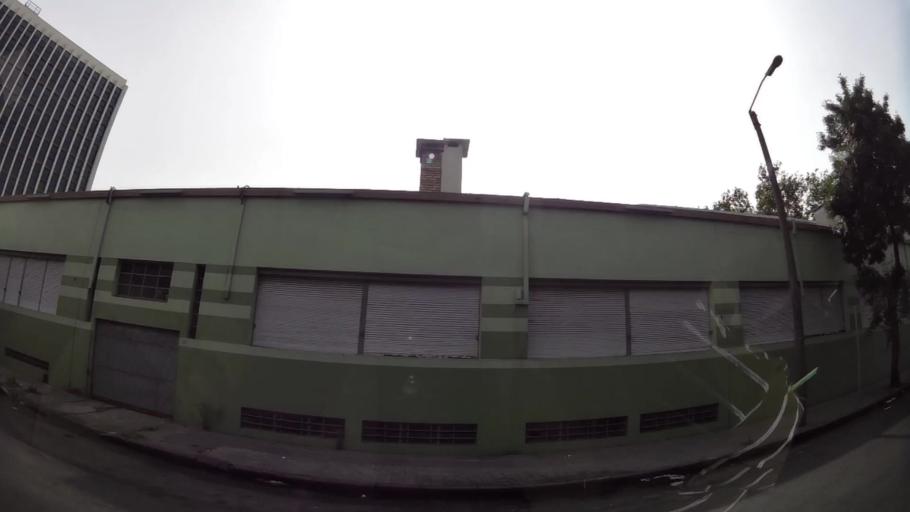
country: UY
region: Montevideo
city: Montevideo
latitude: -34.8865
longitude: -56.1949
